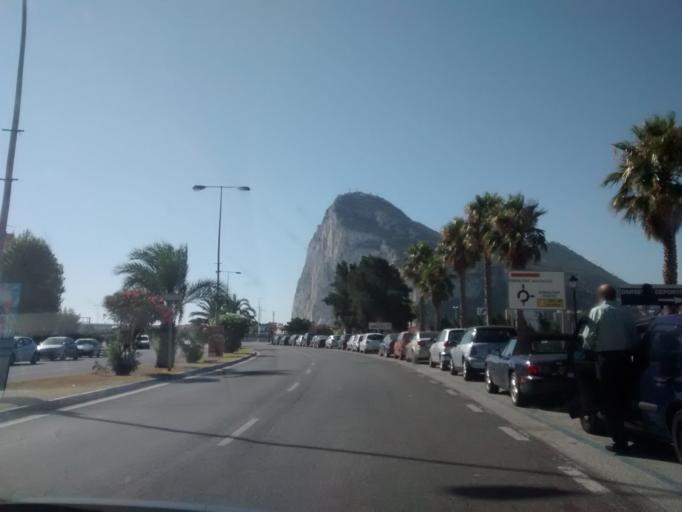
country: ES
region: Andalusia
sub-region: Provincia de Cadiz
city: La Linea de la Concepcion
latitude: 36.1572
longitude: -5.3528
